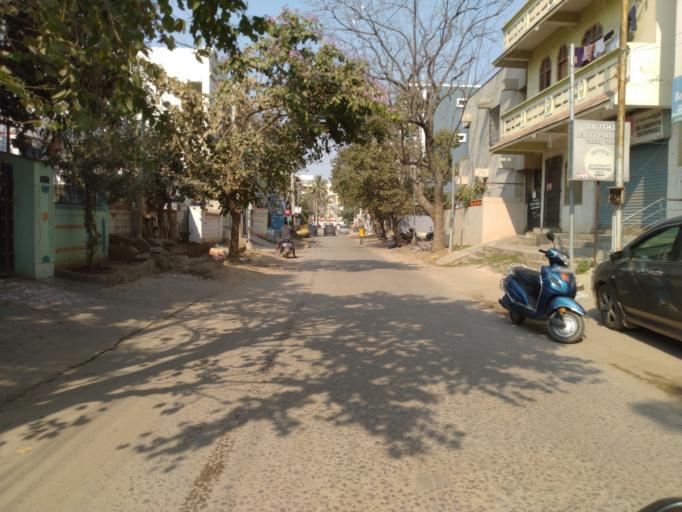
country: IN
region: Telangana
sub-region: Rangareddi
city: Quthbullapur
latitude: 17.5005
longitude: 78.4712
